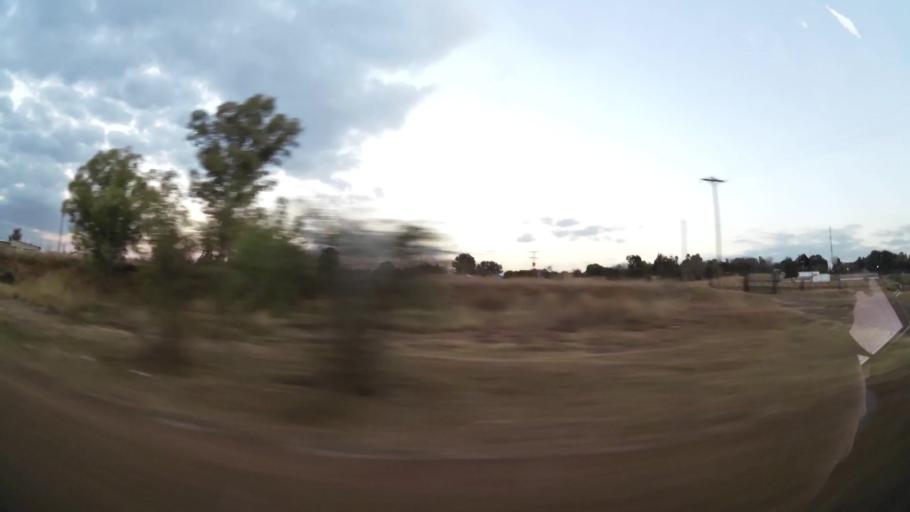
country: ZA
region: Gauteng
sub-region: West Rand District Municipality
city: Krugersdorp
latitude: -26.0664
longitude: 27.6907
